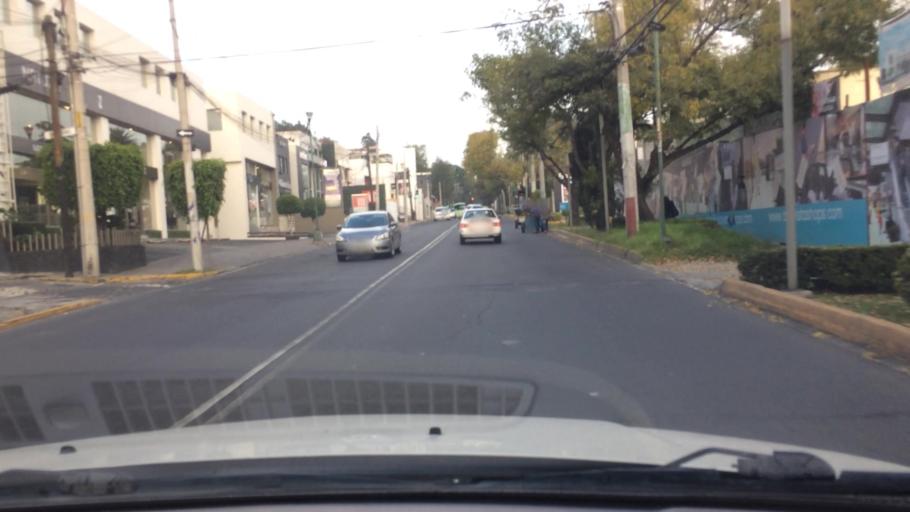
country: MX
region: Mexico City
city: Alvaro Obregon
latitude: 19.3483
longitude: -99.1925
